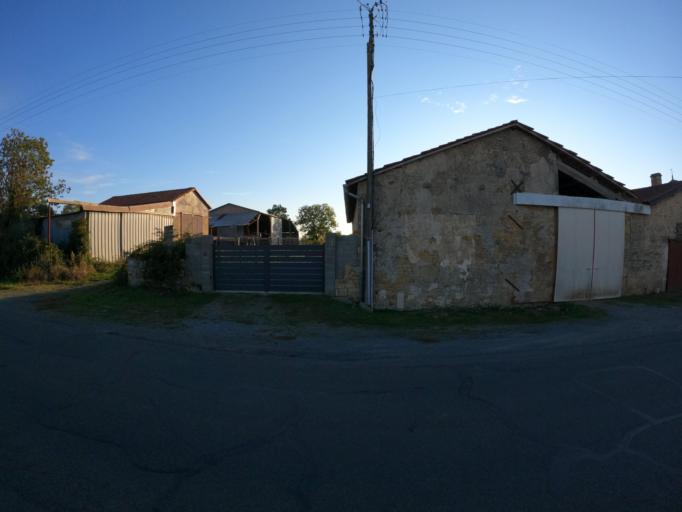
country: FR
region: Pays de la Loire
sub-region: Departement de la Vendee
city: Sainte-Hermine
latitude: 46.5534
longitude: -1.0481
